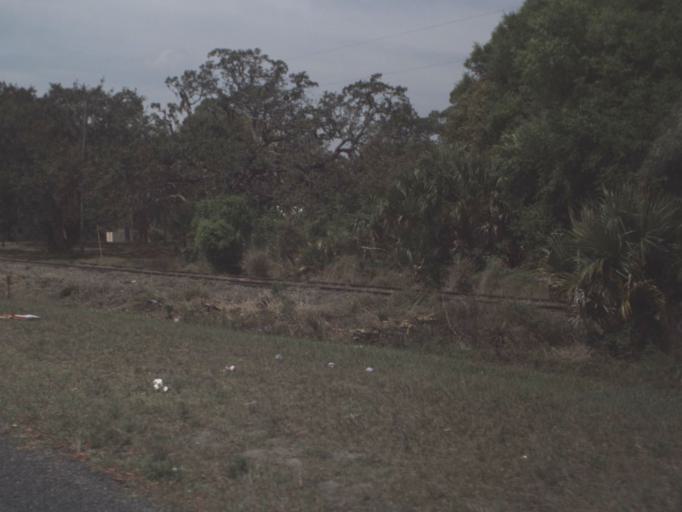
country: US
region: Florida
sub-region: Lake County
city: Umatilla
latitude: 28.9047
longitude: -81.6824
